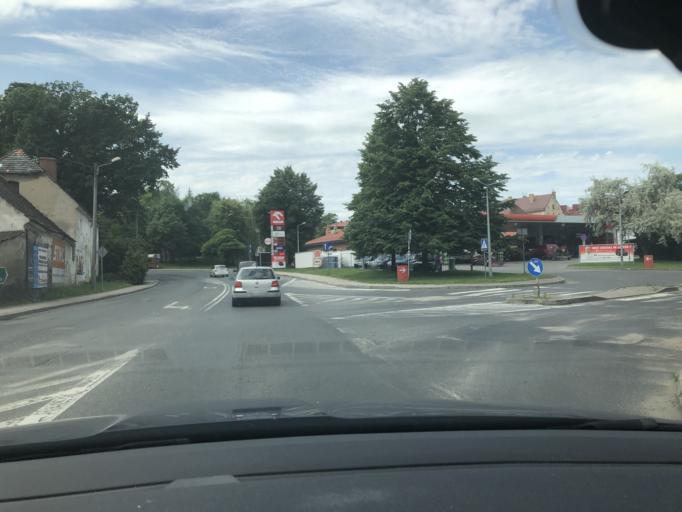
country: PL
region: Lower Silesian Voivodeship
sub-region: Powiat zlotoryjski
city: Zlotoryja
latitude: 51.1261
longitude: 15.9226
